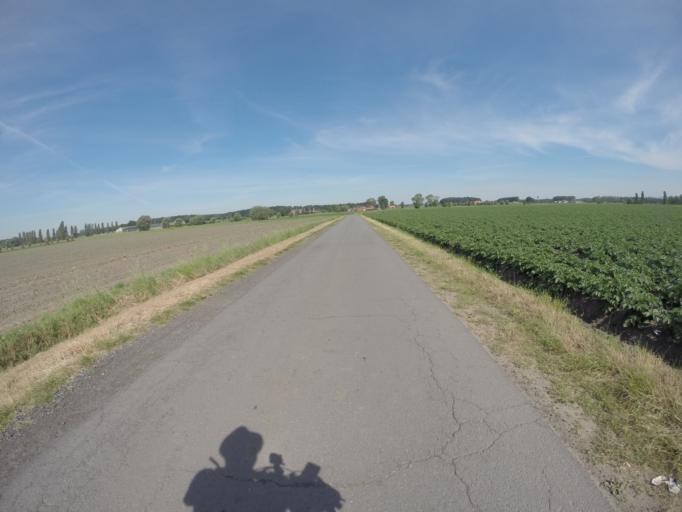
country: BE
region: Flanders
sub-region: Provincie Oost-Vlaanderen
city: Knesselare
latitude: 51.1529
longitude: 3.4077
